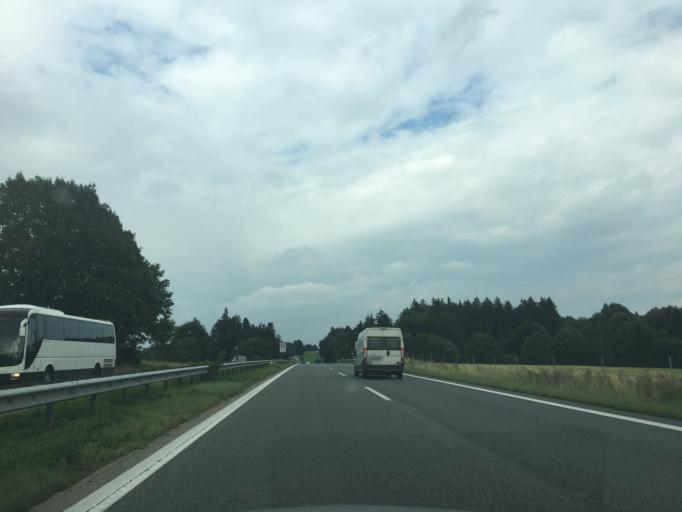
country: DE
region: Bavaria
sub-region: Upper Bavaria
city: Aschau im Chiemgau
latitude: 47.8044
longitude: 12.3238
